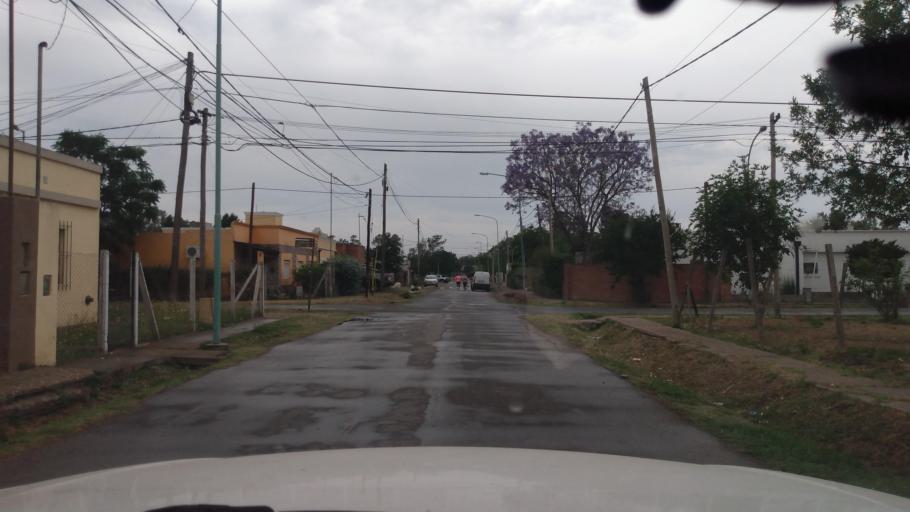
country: AR
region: Buenos Aires
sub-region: Partido de Lujan
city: Lujan
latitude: -34.5555
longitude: -59.2035
